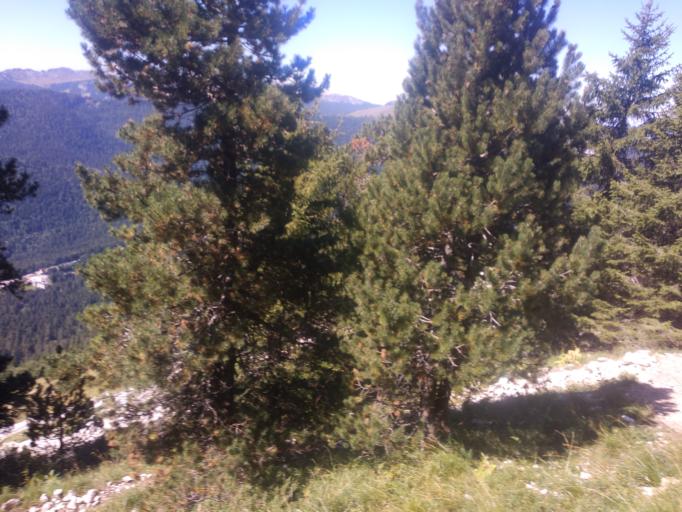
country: FR
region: Rhone-Alpes
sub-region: Departement de l'Isere
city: Le Sappey-en-Chartreuse
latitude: 45.2864
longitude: 5.7825
